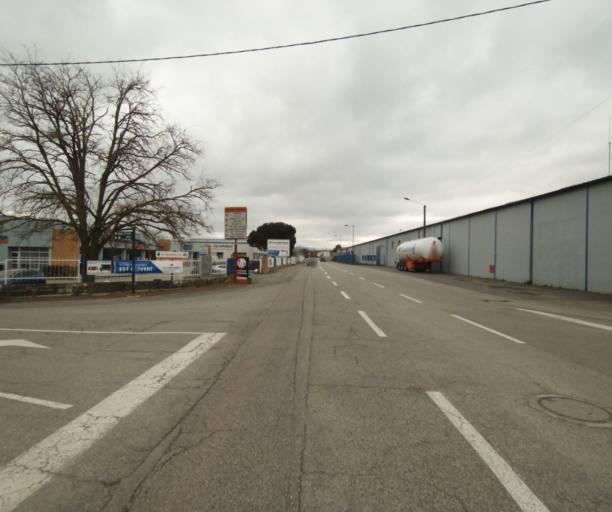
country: FR
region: Midi-Pyrenees
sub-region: Departement de l'Ariege
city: Pamiers
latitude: 43.1214
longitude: 1.6212
